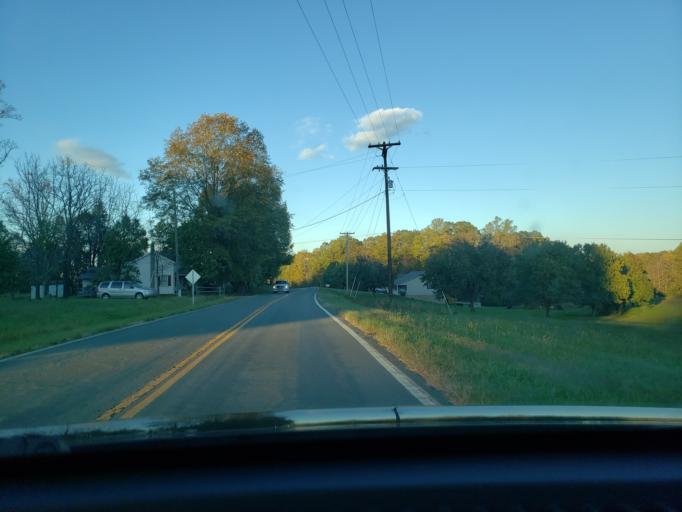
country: US
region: North Carolina
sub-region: Stokes County
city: Danbury
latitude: 36.3679
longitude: -80.1914
